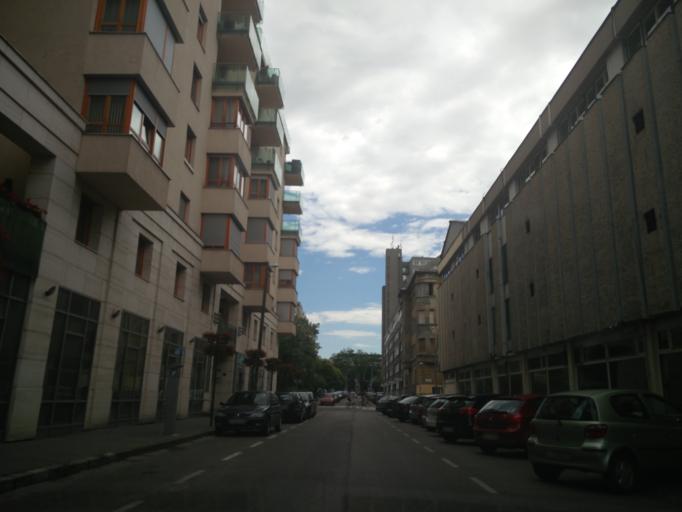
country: HU
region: Budapest
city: Budapest VI. keruelet
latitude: 47.5219
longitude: 19.0589
